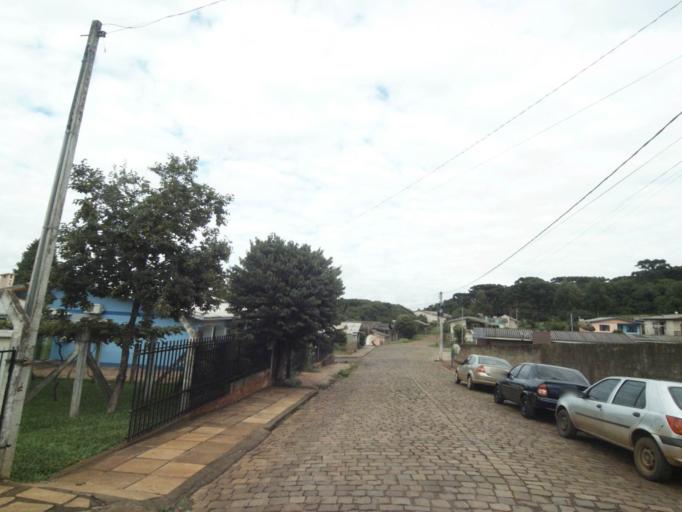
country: BR
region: Rio Grande do Sul
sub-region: Lagoa Vermelha
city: Lagoa Vermelha
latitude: -28.2208
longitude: -51.5222
